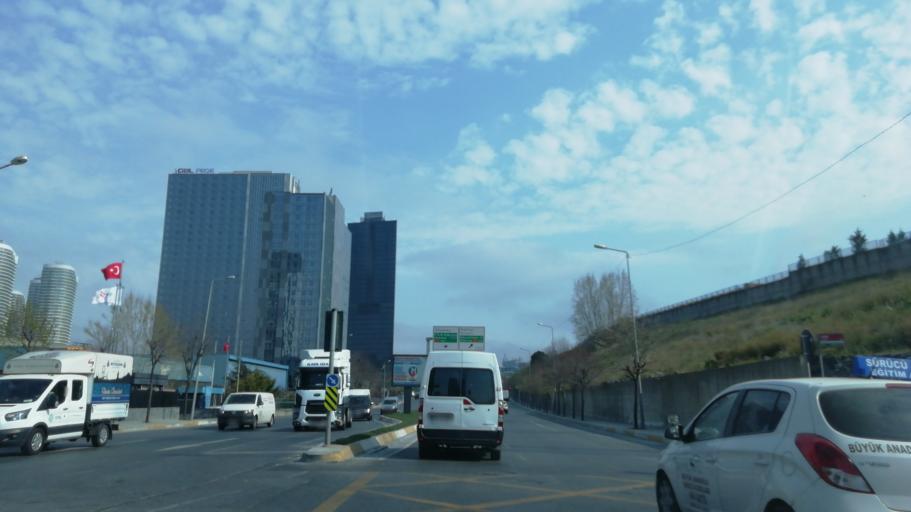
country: TR
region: Istanbul
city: Mahmutbey
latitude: 41.0555
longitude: 28.8131
